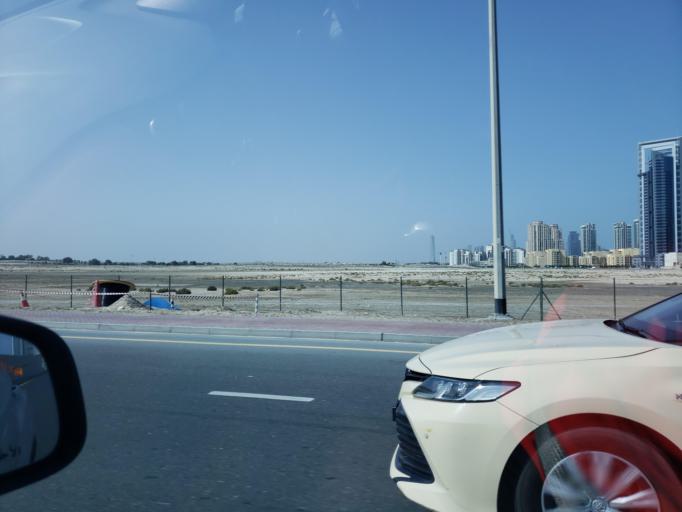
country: AE
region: Dubai
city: Dubai
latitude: 25.0947
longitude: 55.1834
